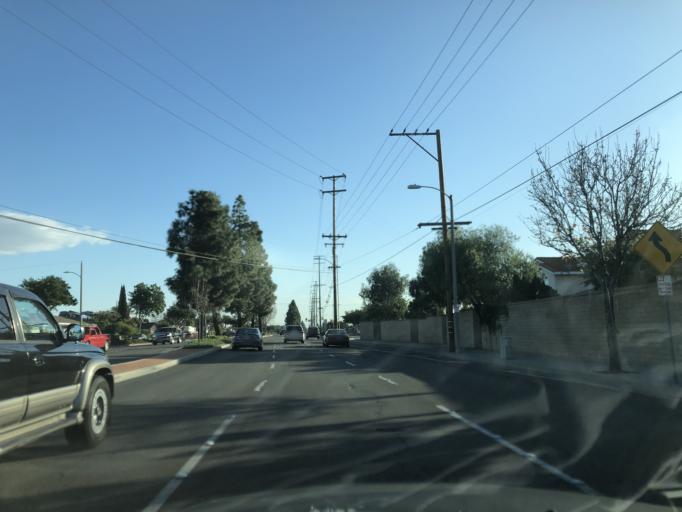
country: US
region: California
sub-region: Orange County
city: La Palma
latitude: 33.8450
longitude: -118.0286
